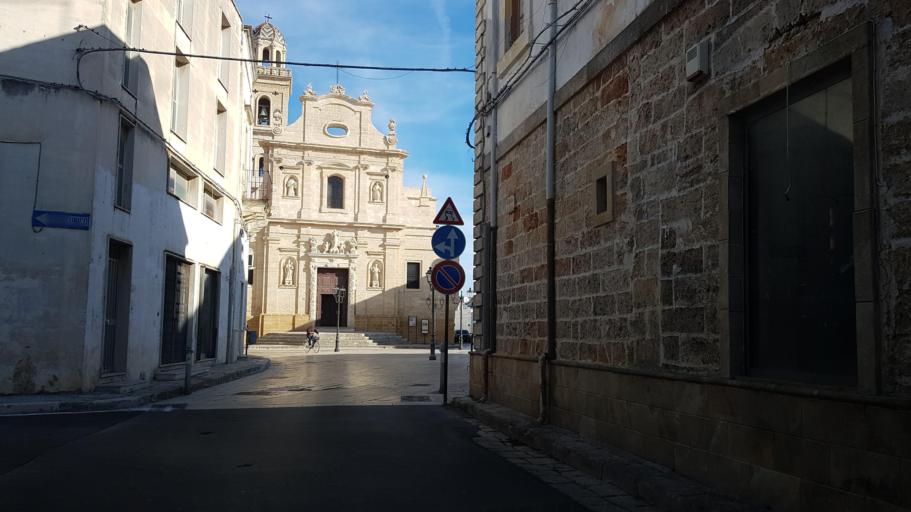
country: IT
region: Apulia
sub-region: Provincia di Lecce
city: Salice Salentino
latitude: 40.3859
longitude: 17.9634
